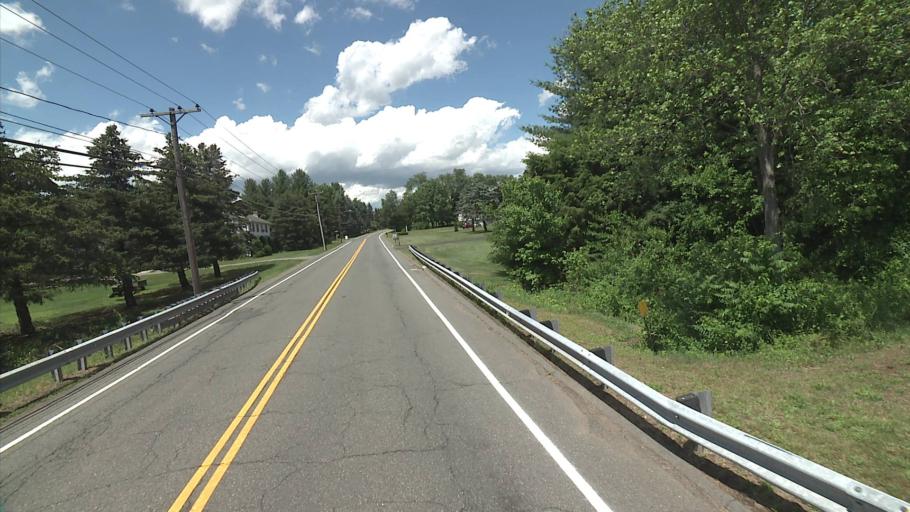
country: US
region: Connecticut
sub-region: Tolland County
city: Somers
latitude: 41.9994
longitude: -72.4882
